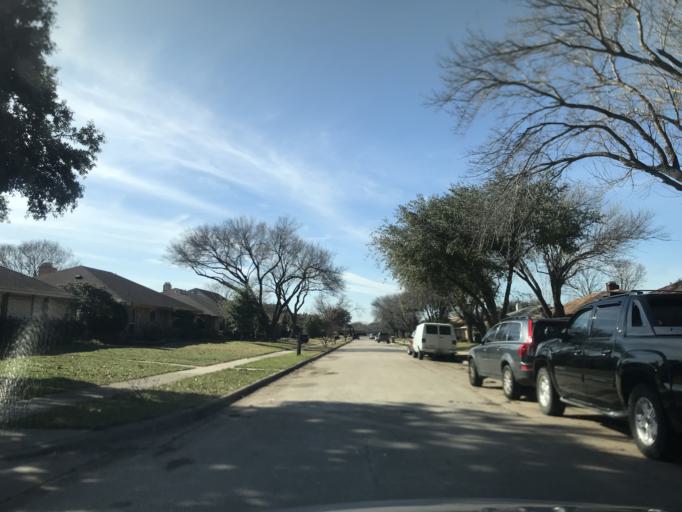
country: US
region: Texas
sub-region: Dallas County
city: Carrollton
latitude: 32.9873
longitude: -96.8718
